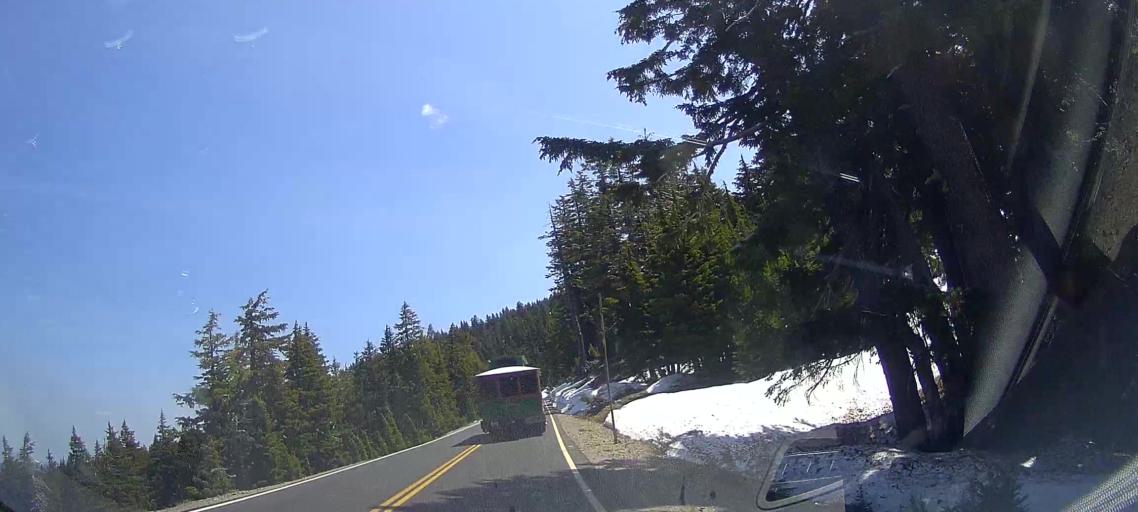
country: US
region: Oregon
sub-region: Jackson County
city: Shady Cove
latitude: 42.9713
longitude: -122.1484
